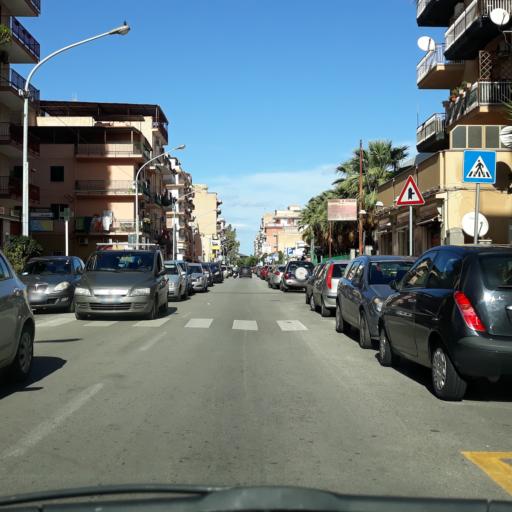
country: IT
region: Sicily
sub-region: Palermo
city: Palermo
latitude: 38.1498
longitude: 13.3708
